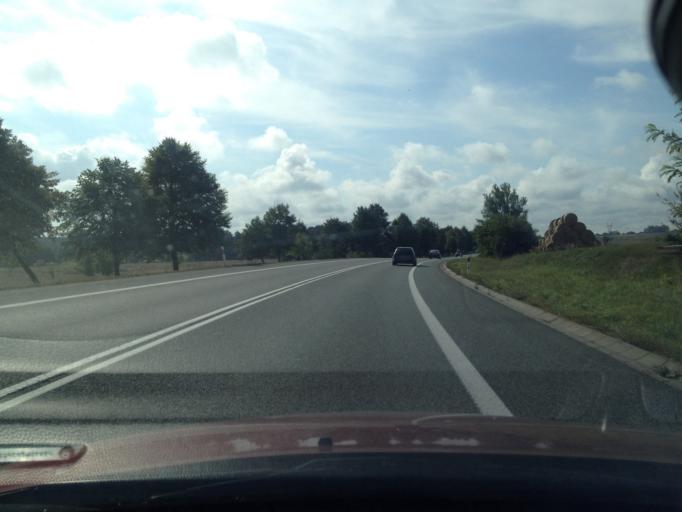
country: PL
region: West Pomeranian Voivodeship
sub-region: Powiat goleniowski
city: Przybiernow
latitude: 53.8092
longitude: 14.7684
